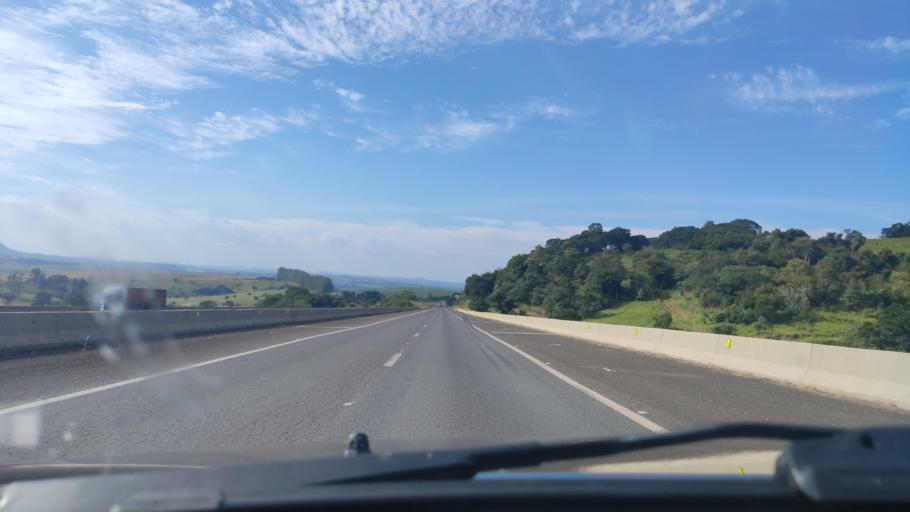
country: BR
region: Sao Paulo
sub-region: Itatinga
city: Itatinga
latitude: -23.1053
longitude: -48.5053
